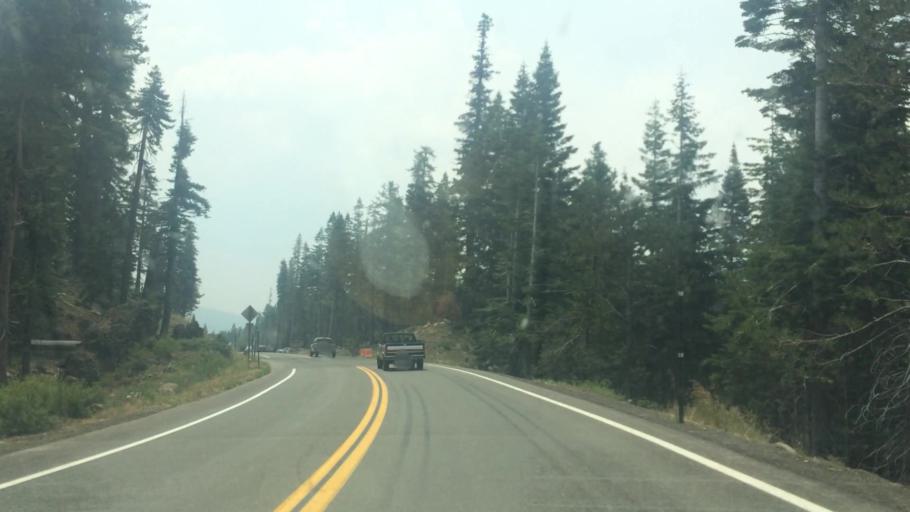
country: US
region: California
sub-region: El Dorado County
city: South Lake Tahoe
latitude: 38.6714
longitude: -120.1213
